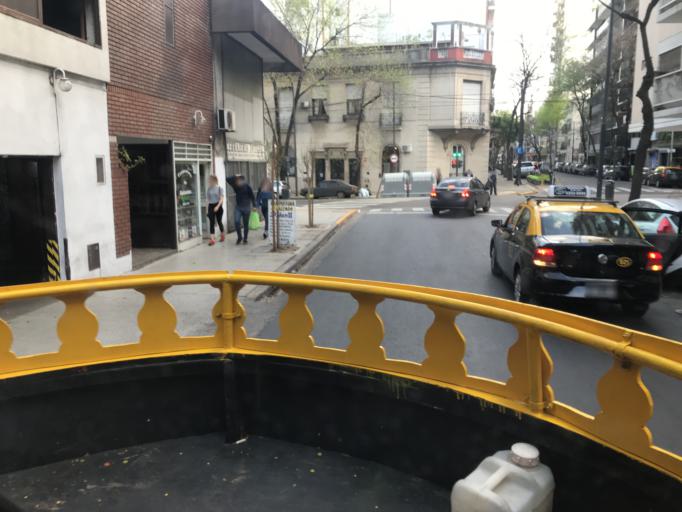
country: AR
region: Buenos Aires F.D.
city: Retiro
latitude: -34.5942
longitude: -58.4089
